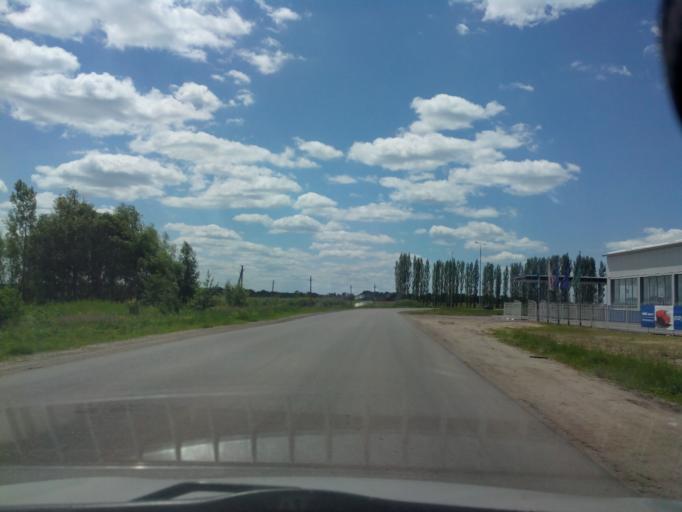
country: RU
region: Voronezj
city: Ternovka
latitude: 51.6772
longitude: 41.5997
